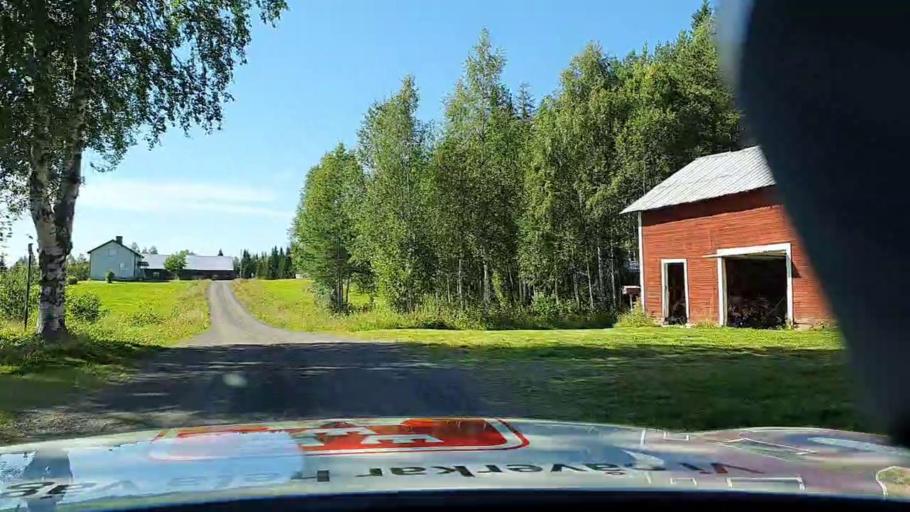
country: SE
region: Jaemtland
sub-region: Krokoms Kommun
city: Krokom
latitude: 63.7758
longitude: 14.6433
